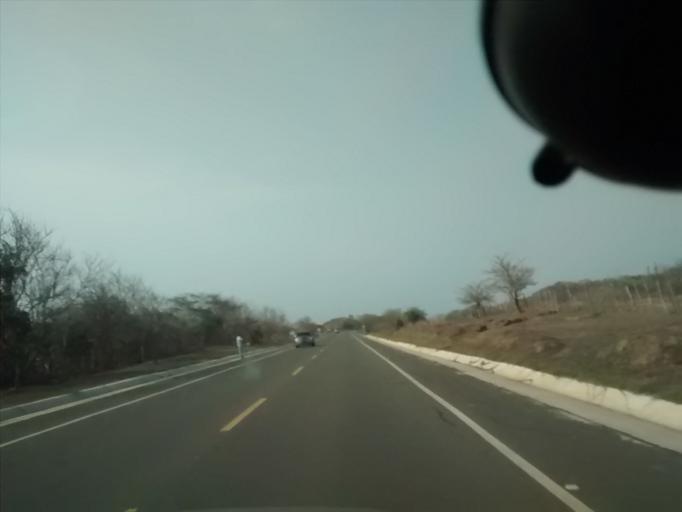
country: CO
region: Atlantico
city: Juan de Acosta
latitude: 10.8526
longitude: -75.1272
